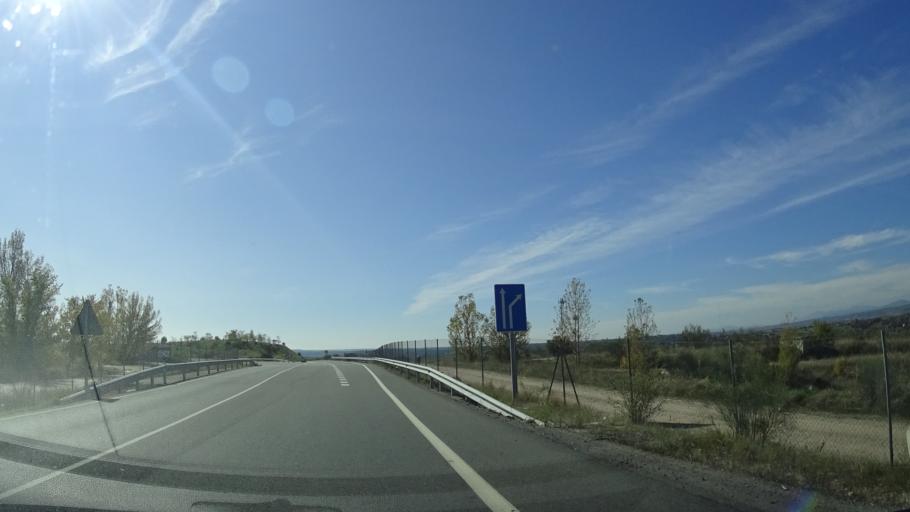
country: ES
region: Madrid
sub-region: Provincia de Madrid
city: Villanueva del Pardillo
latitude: 40.4854
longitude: -3.9221
